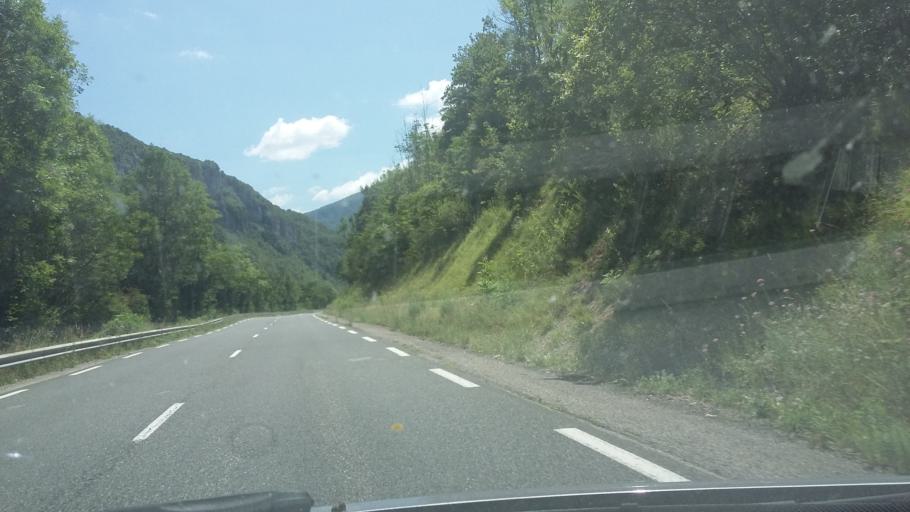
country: FR
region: Rhone-Alpes
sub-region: Departement de l'Ain
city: Tenay
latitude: 45.8654
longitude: 5.5357
